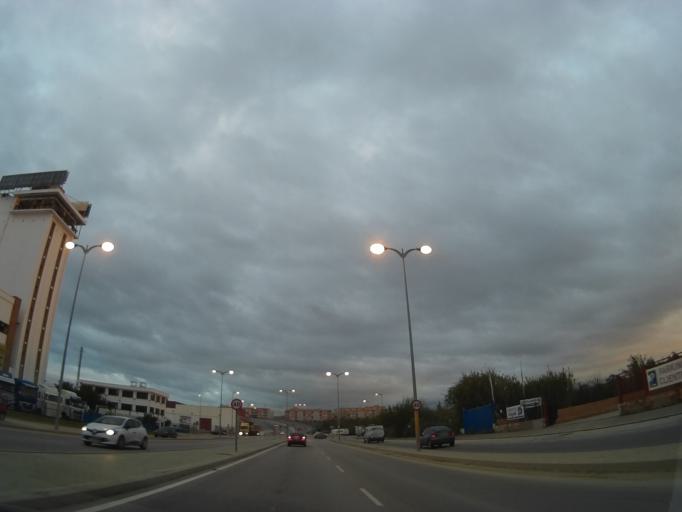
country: ES
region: Andalusia
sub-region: Provincia de Malaga
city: Malaga
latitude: 36.6992
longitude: -4.4925
